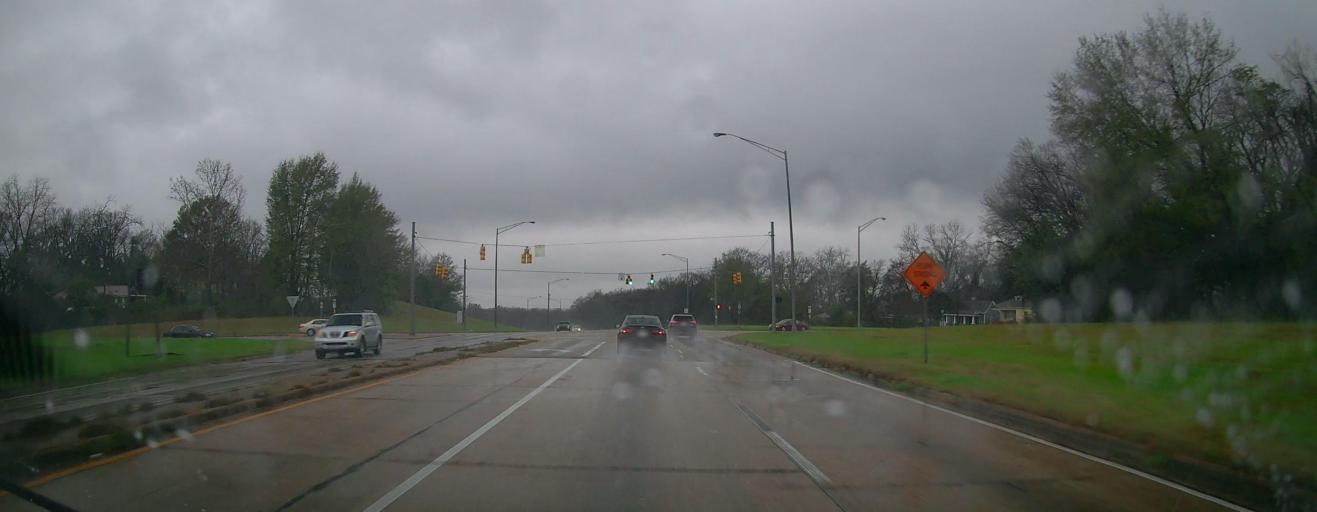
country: US
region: Alabama
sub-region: Montgomery County
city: Montgomery
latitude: 32.3685
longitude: -86.3285
